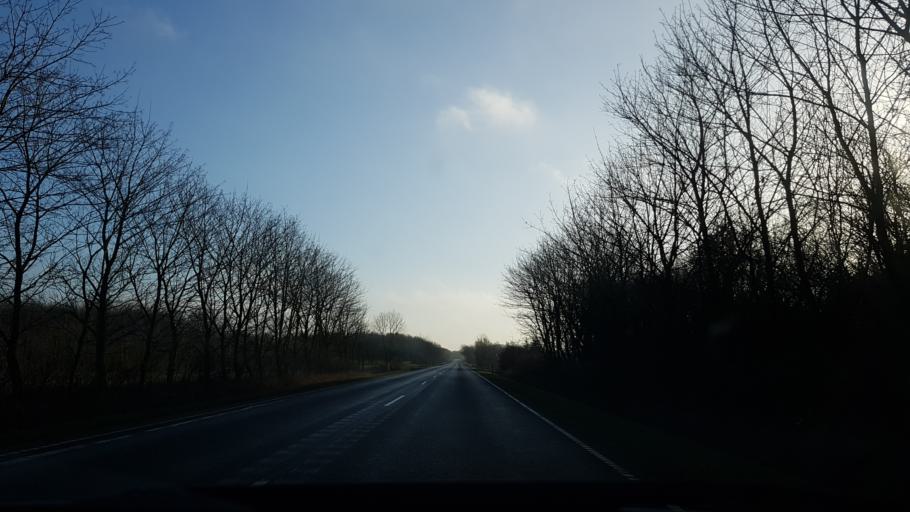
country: DK
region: South Denmark
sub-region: Haderslev Kommune
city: Vojens
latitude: 55.2074
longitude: 9.1903
